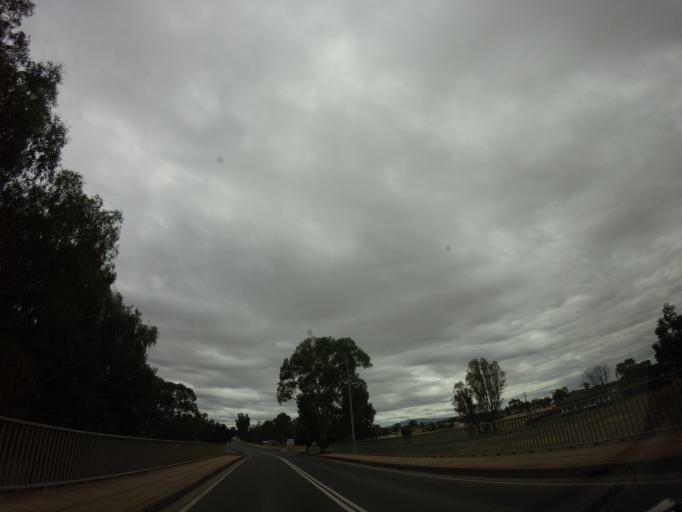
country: AU
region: New South Wales
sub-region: Narrabri
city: Narrabri
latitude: -30.3331
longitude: 149.7727
